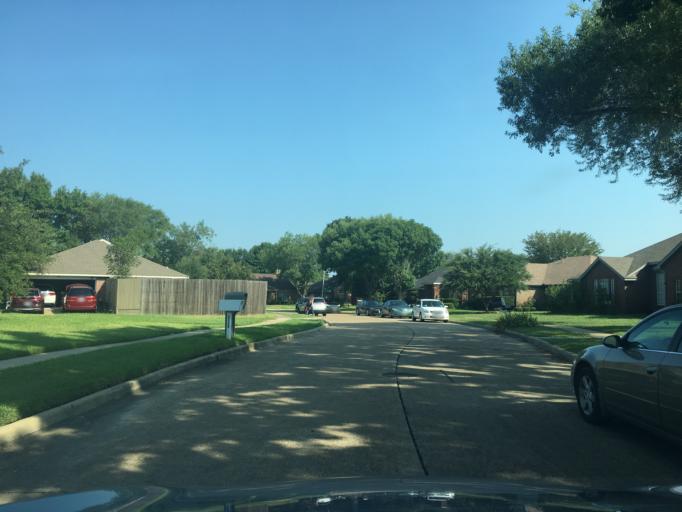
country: US
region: Texas
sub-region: Dallas County
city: Garland
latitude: 32.9421
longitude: -96.6242
